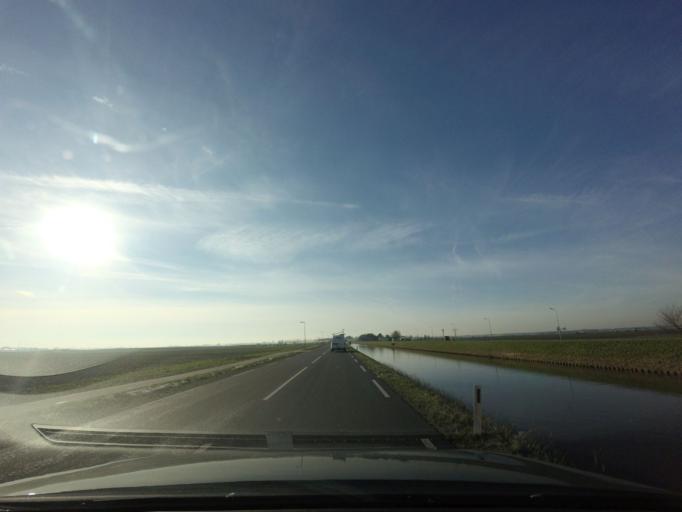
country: NL
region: North Holland
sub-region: Gemeente Haarlemmermeer
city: Hoofddorp
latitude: 52.3403
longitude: 4.7430
